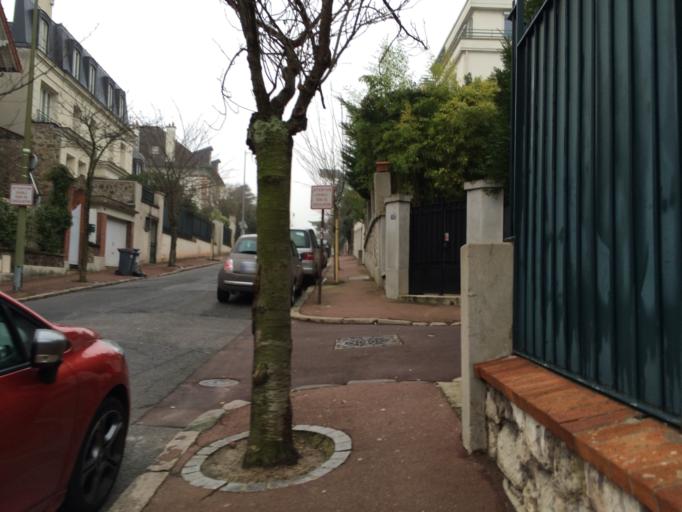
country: FR
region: Ile-de-France
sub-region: Departement des Hauts-de-Seine
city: Suresnes
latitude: 48.8586
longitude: 2.2174
